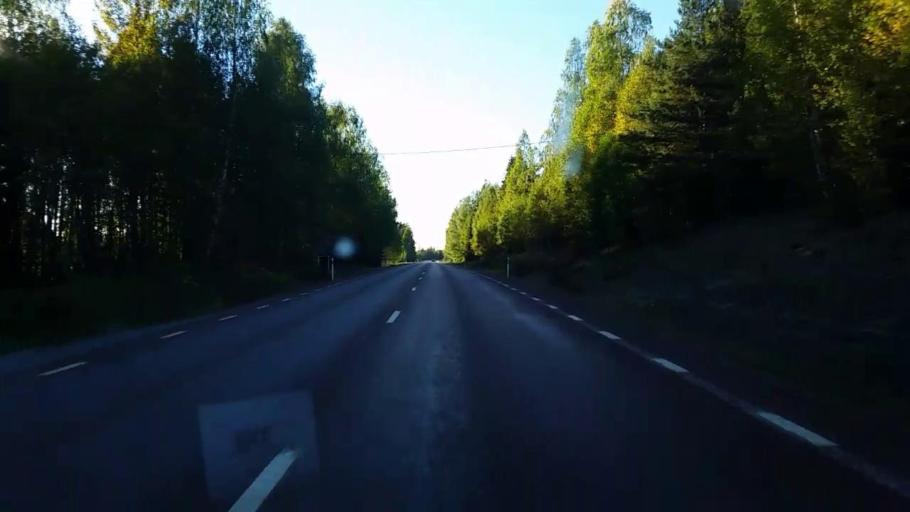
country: SE
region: Gaevleborg
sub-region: Ljusdals Kommun
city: Ljusdal
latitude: 61.8183
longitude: 16.1818
